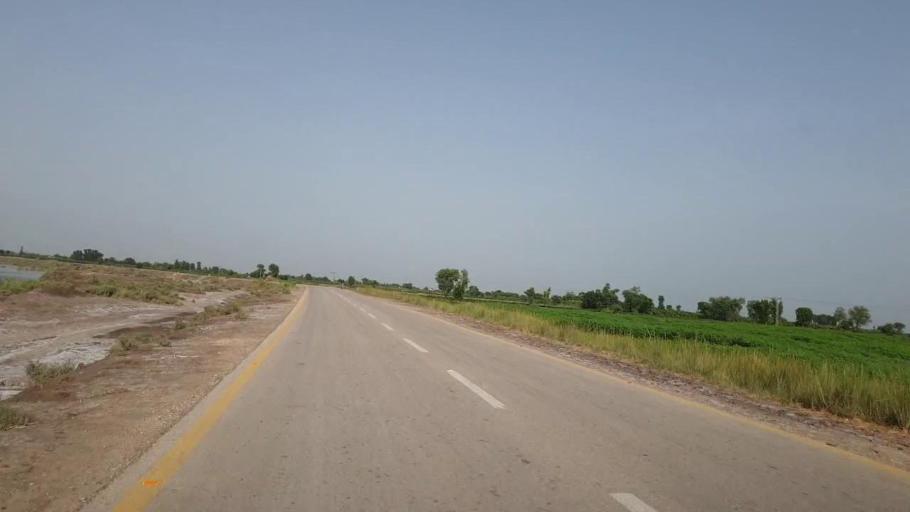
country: PK
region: Sindh
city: Bandhi
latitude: 26.5779
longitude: 68.2733
